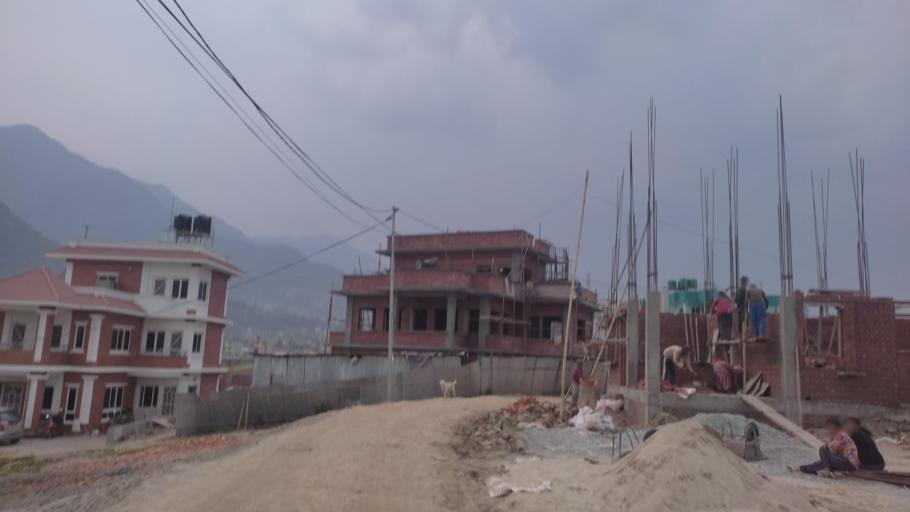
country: NP
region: Central Region
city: Kirtipur
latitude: 27.6626
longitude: 85.2751
